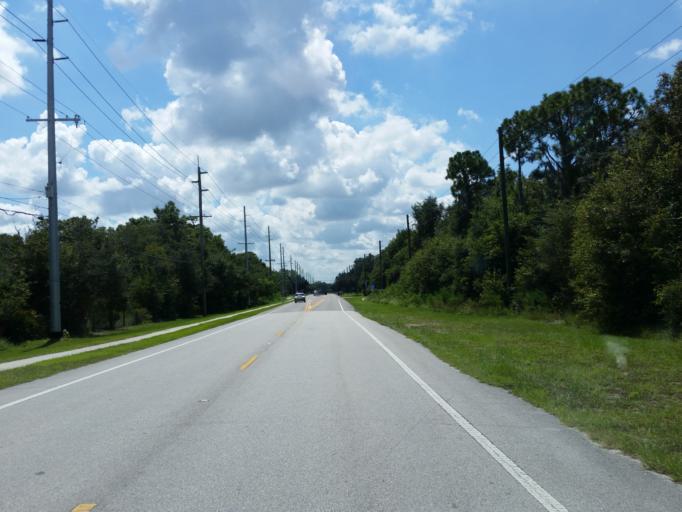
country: US
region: Florida
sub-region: Hillsborough County
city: Riverview
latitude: 27.8408
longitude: -82.3020
